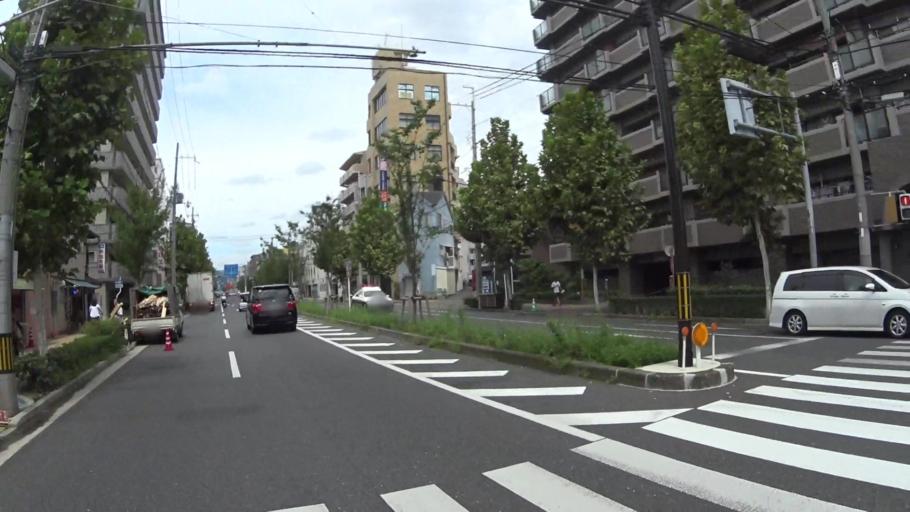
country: JP
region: Kyoto
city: Kyoto
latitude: 35.0064
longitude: 135.7319
